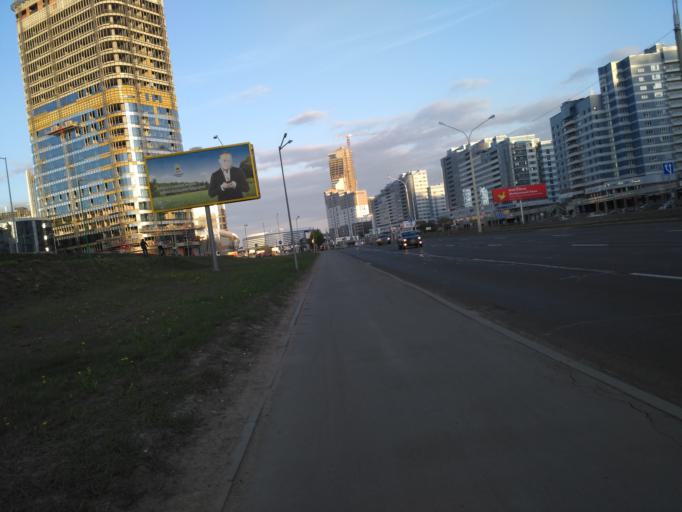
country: BY
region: Minsk
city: Zhdanovichy
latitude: 53.9417
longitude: 27.4676
